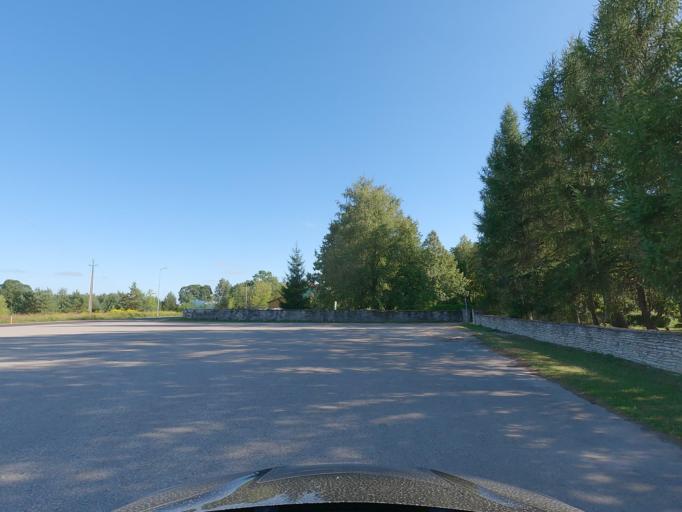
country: EE
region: Raplamaa
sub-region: Rapla vald
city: Rapla
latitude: 59.0140
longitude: 24.7841
